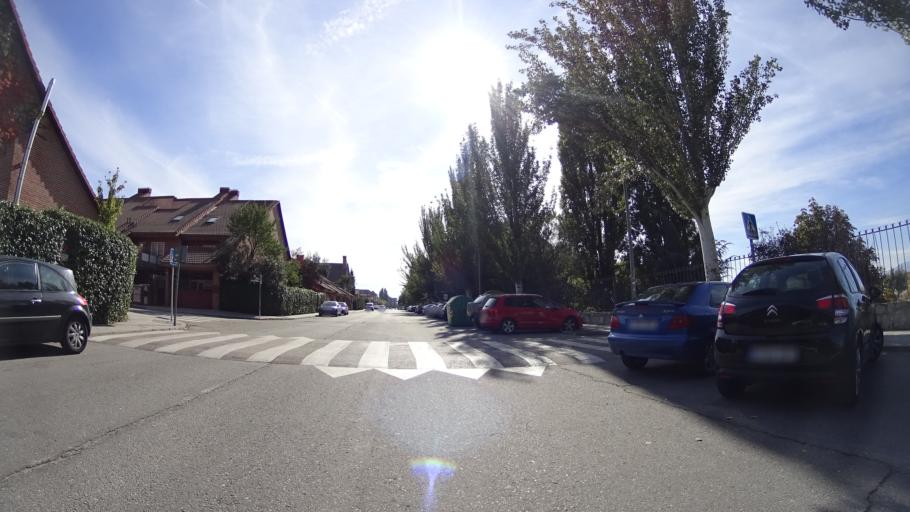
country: ES
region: Madrid
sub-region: Provincia de Madrid
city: Collado-Villalba
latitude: 40.6229
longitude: -4.0159
